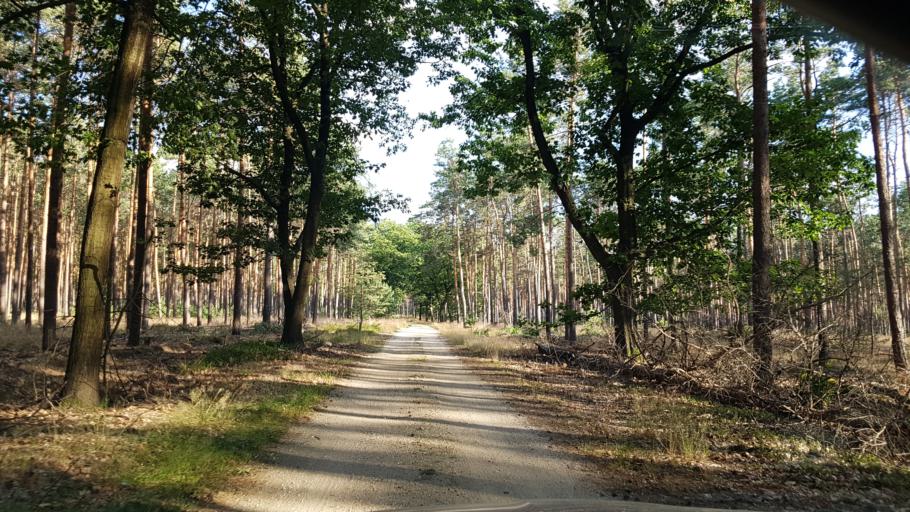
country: DE
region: Brandenburg
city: Trobitz
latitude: 51.6286
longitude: 13.4092
